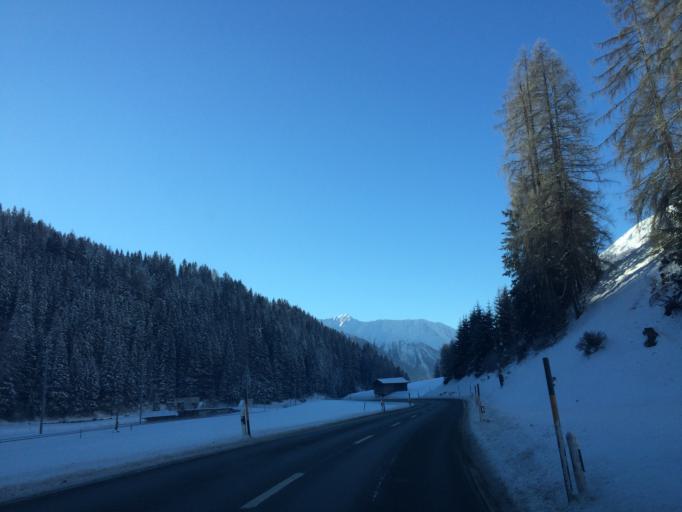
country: CH
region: Grisons
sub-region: Praettigau/Davos District
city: Davos
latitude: 46.7557
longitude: 9.7866
